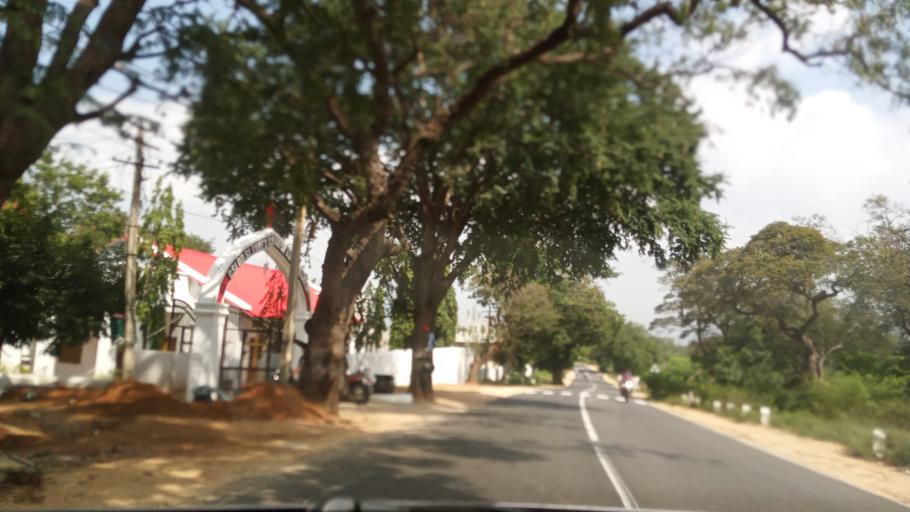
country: IN
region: Andhra Pradesh
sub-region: Chittoor
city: Madanapalle
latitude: 13.6019
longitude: 78.5325
